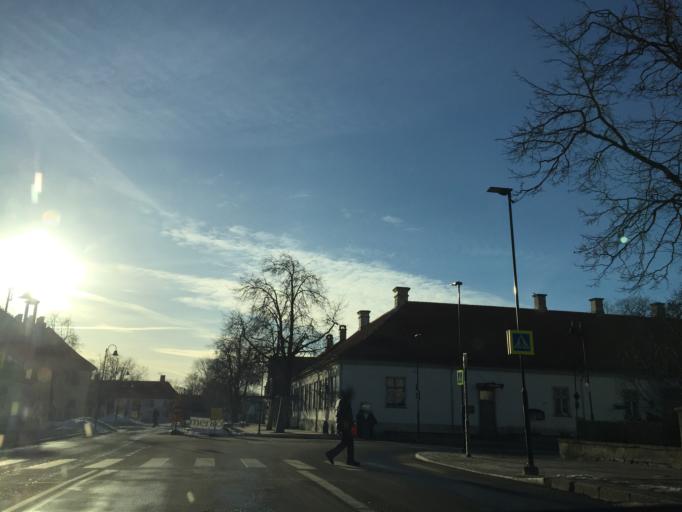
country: EE
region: Saare
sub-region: Kuressaare linn
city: Kuressaare
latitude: 58.2534
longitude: 22.4871
